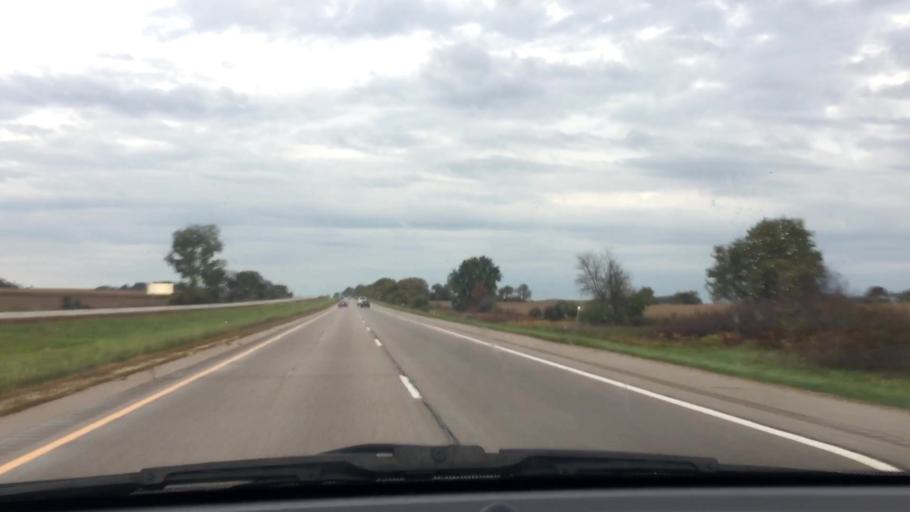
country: US
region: Wisconsin
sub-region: Rock County
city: Clinton
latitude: 42.5727
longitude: -88.8408
